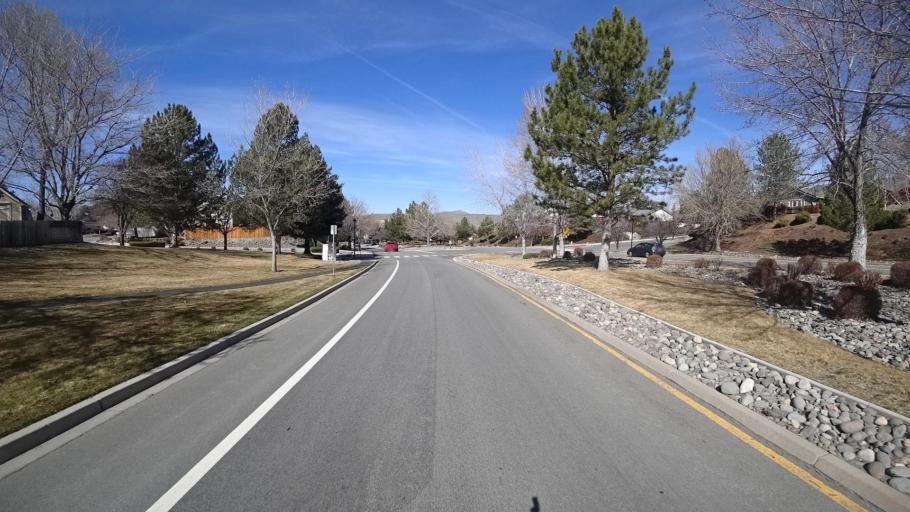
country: US
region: Nevada
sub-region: Washoe County
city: Spanish Springs
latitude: 39.5842
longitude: -119.7055
